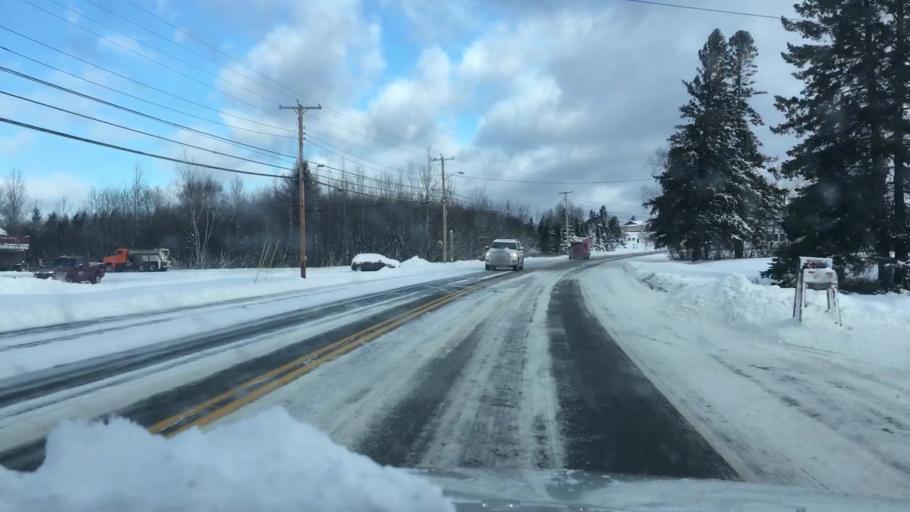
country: US
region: Maine
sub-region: Aroostook County
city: Caribou
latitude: 46.9303
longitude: -68.0232
